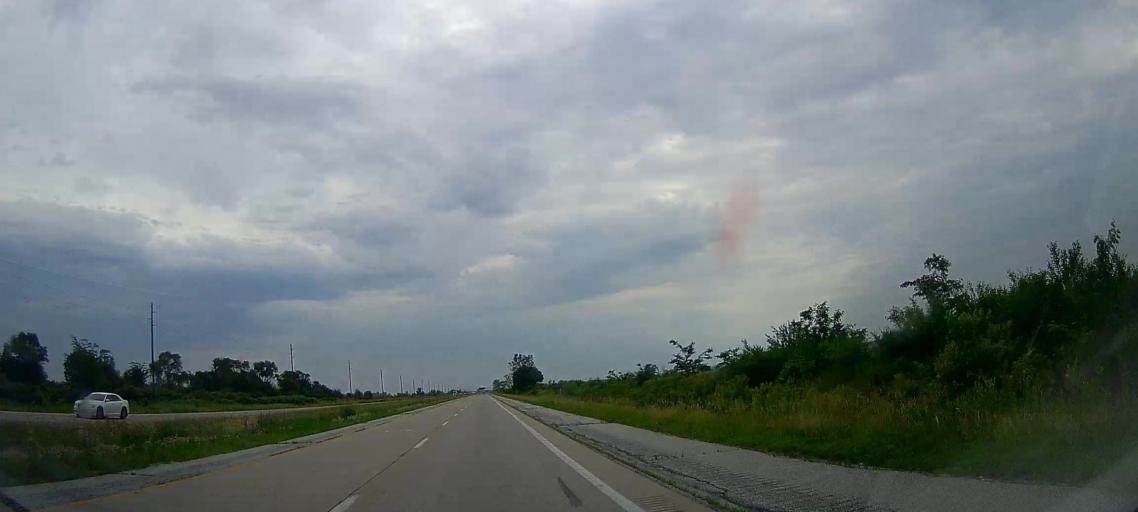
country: US
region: Iowa
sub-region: Pottawattamie County
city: Carter Lake
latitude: 41.3926
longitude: -95.8998
